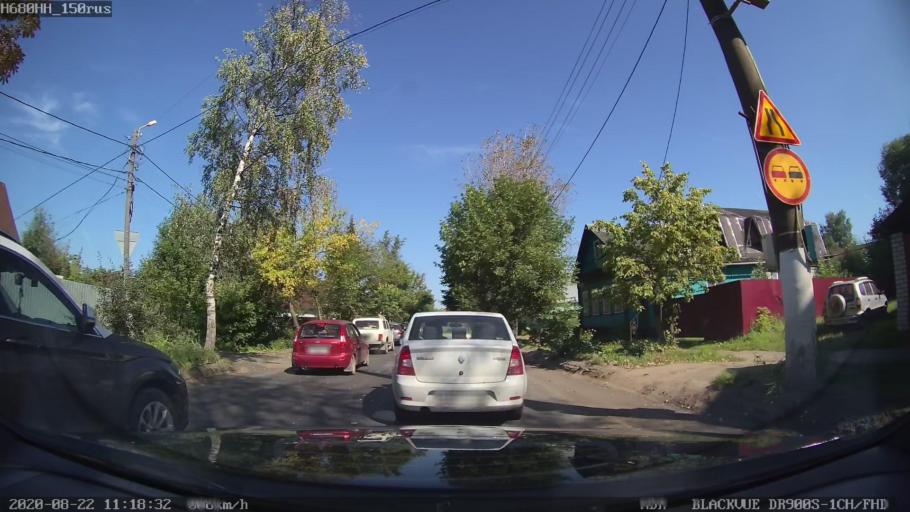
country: RU
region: Tverskaya
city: Tver
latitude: 56.8757
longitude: 35.9289
